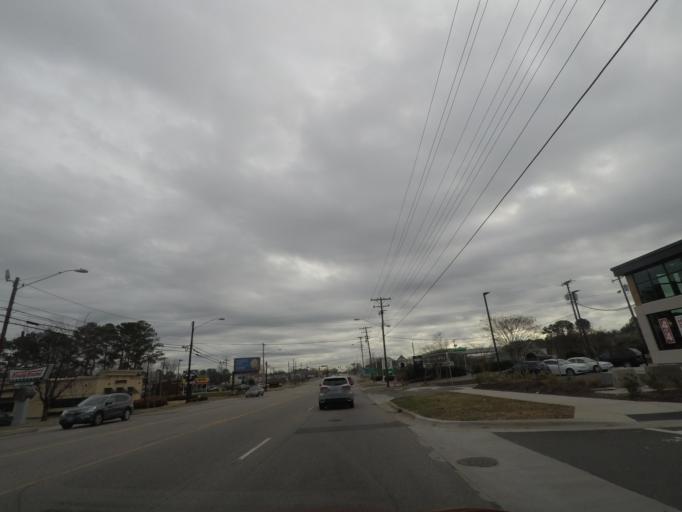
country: US
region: North Carolina
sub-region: Durham County
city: Durham
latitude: 36.0215
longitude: -78.9516
